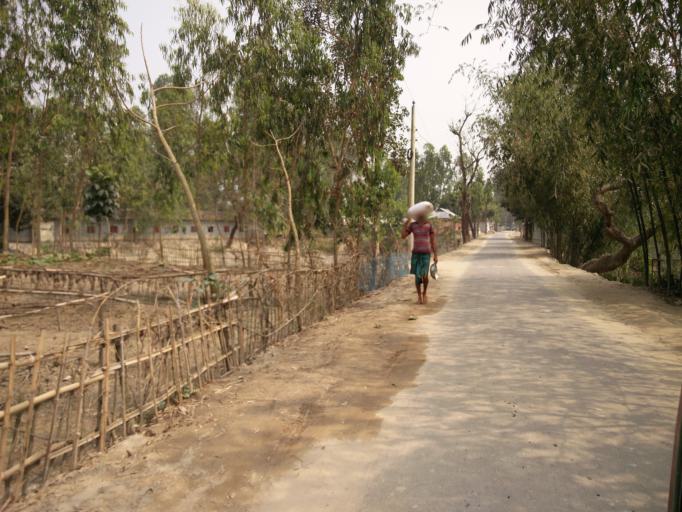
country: BD
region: Rangpur Division
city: Nageswari
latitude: 25.8866
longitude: 89.7369
